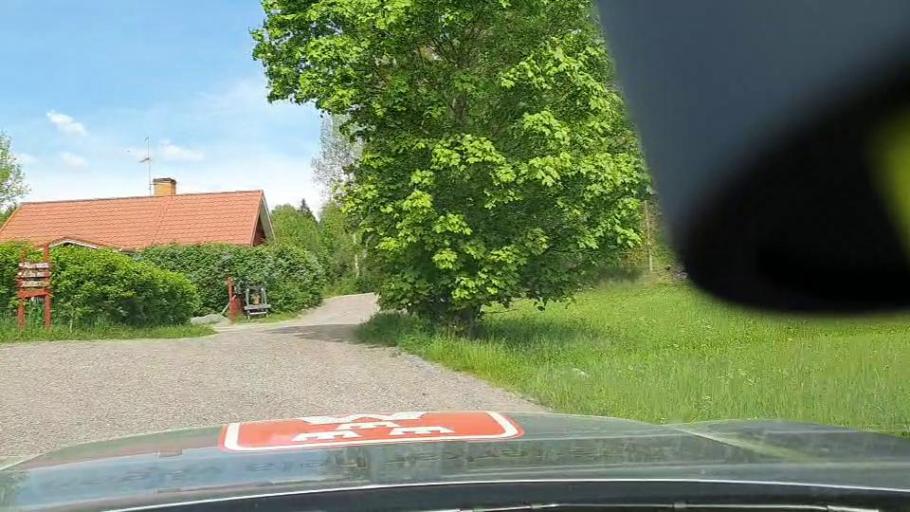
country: SE
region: Soedermanland
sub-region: Eskilstuna Kommun
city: Skogstorp
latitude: 59.2532
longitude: 16.5036
